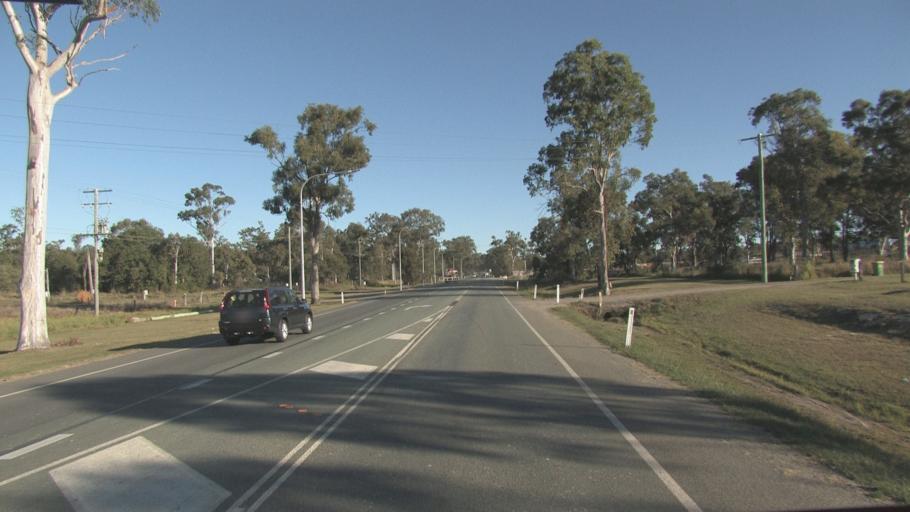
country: AU
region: Queensland
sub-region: Logan
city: Logan Reserve
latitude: -27.7167
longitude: 153.0921
